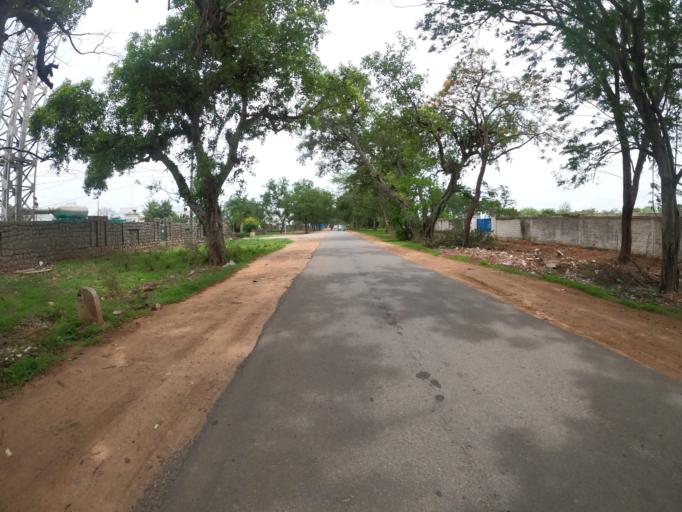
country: IN
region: Telangana
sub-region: Hyderabad
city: Hyderabad
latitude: 17.3438
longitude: 78.3743
